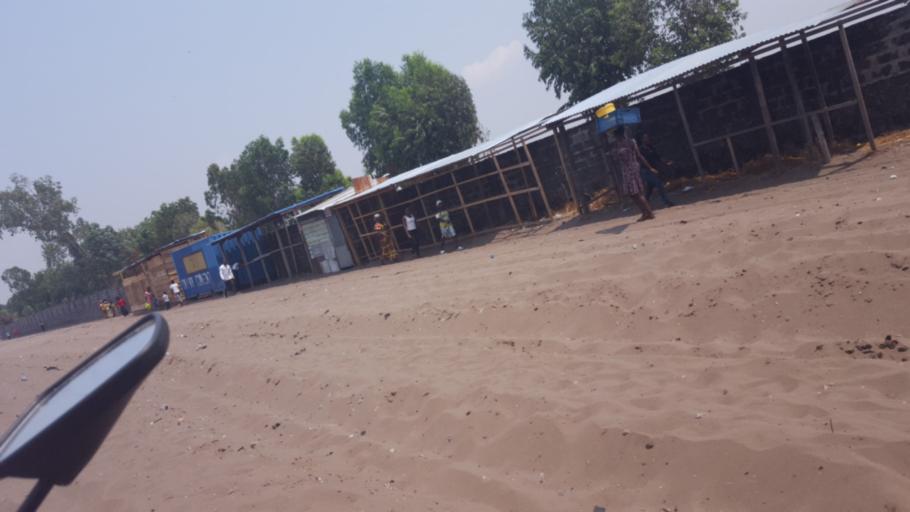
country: CD
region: Kinshasa
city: Masina
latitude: -4.3594
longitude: 15.5070
